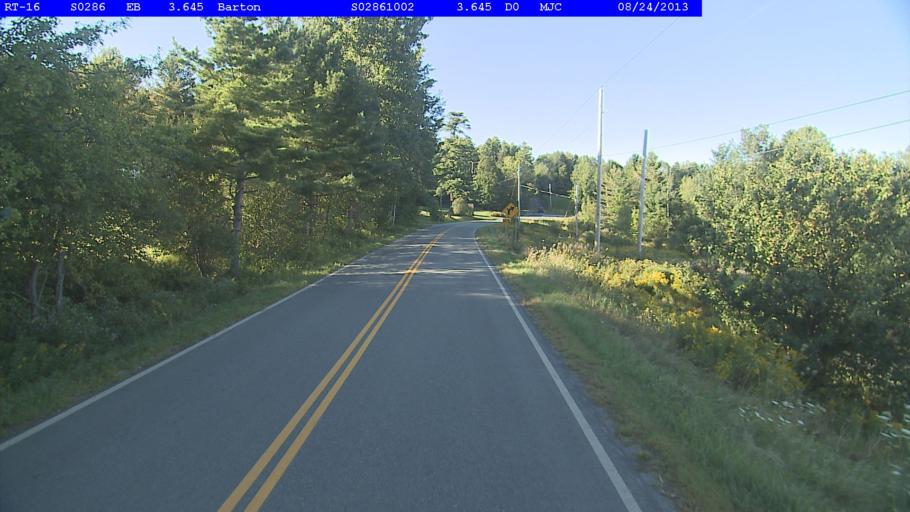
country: US
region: Vermont
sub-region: Orleans County
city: Newport
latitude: 44.7749
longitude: -72.1291
